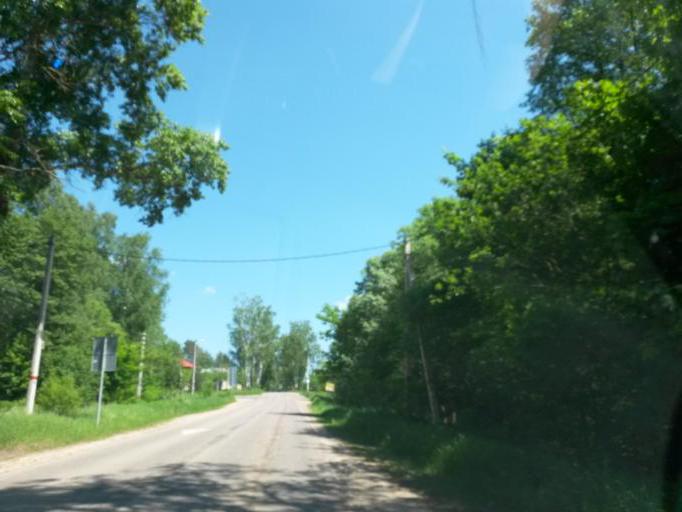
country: RU
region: Moskovskaya
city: Danki
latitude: 54.9108
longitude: 37.5592
